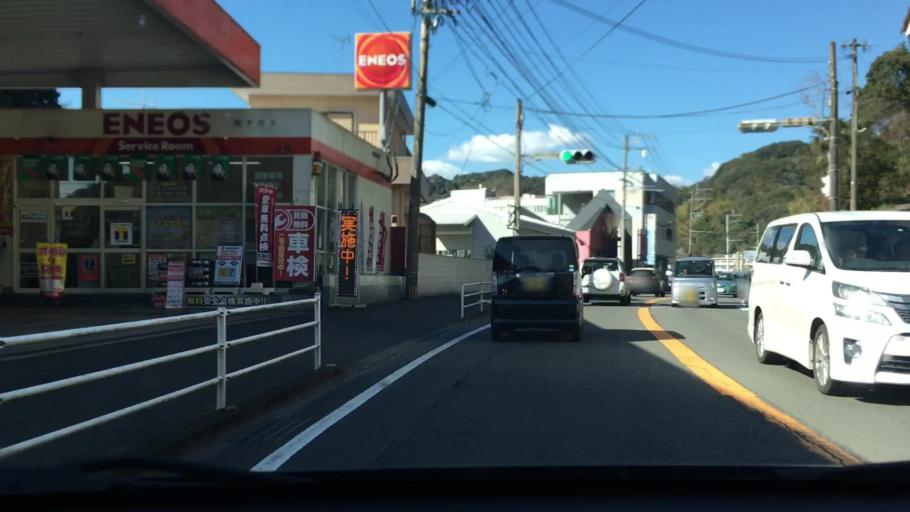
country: JP
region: Kagoshima
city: Kagoshima-shi
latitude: 31.6398
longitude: 130.5170
